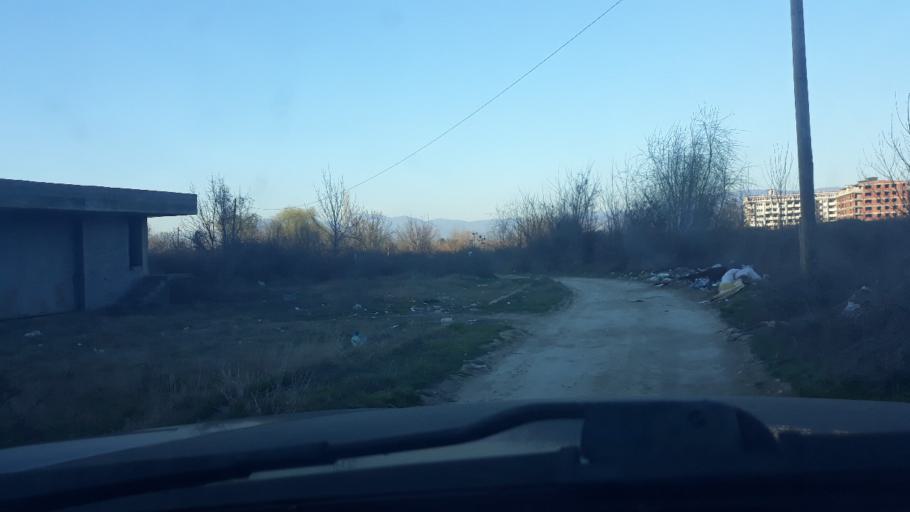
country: MK
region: Strumica
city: Strumica
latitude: 41.4410
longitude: 22.6260
